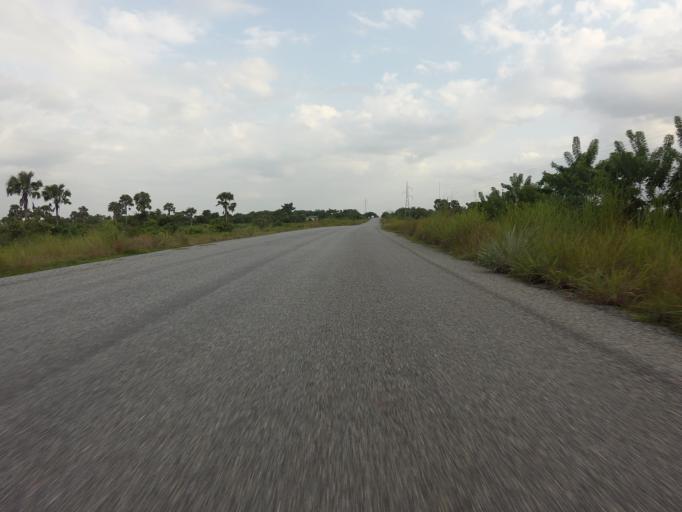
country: GH
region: Volta
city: Ho
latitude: 6.3984
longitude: 0.5255
